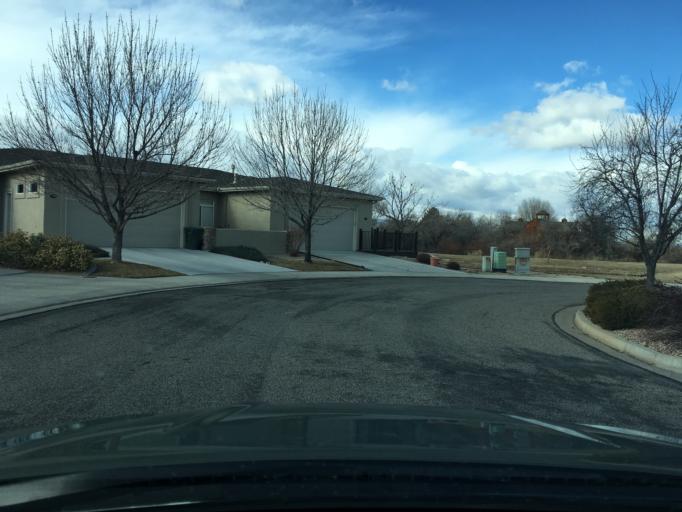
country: US
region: Colorado
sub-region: Mesa County
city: Grand Junction
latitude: 39.1275
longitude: -108.5585
